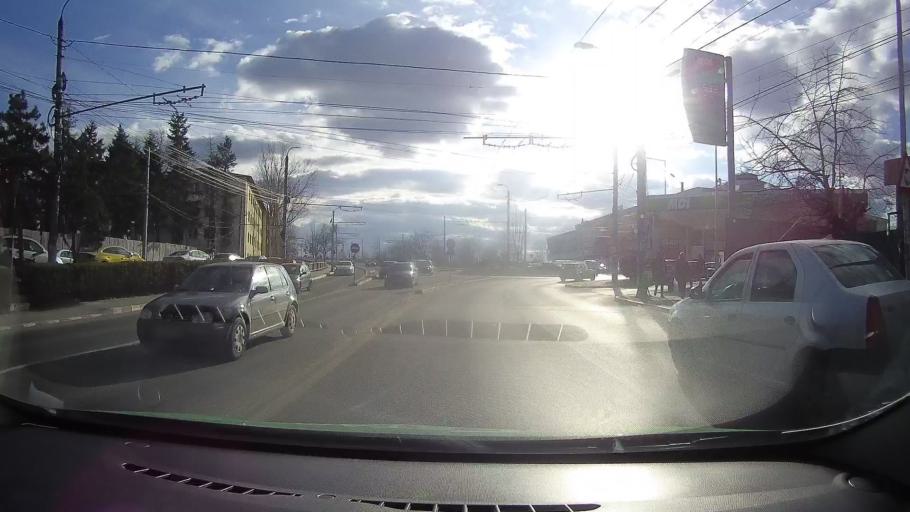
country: RO
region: Dambovita
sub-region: Comuna Lucieni
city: Lucieni
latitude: 44.8551
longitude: 25.4217
